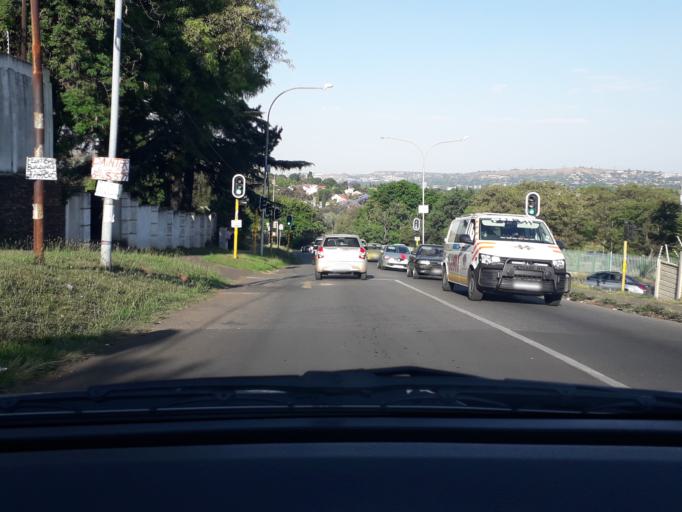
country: ZA
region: Gauteng
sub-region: City of Johannesburg Metropolitan Municipality
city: Johannesburg
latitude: -26.1803
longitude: 28.0878
